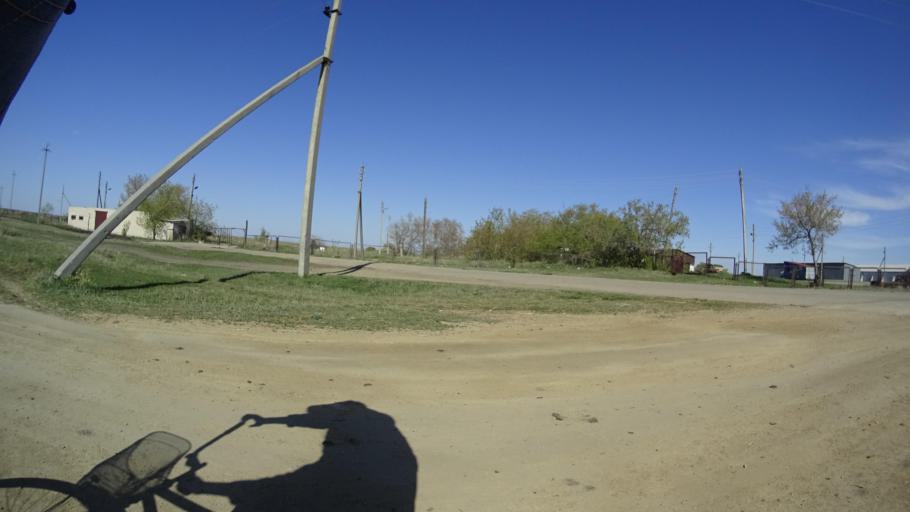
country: RU
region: Chelyabinsk
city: Chesma
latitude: 53.7958
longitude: 61.0358
